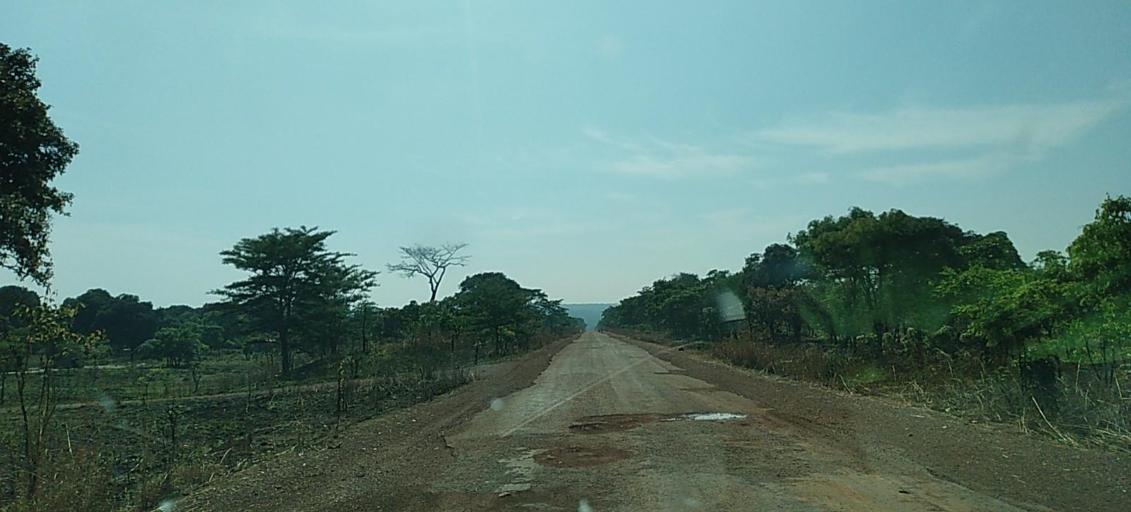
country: ZM
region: North-Western
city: Mwinilunga
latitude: -11.8220
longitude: 25.1043
